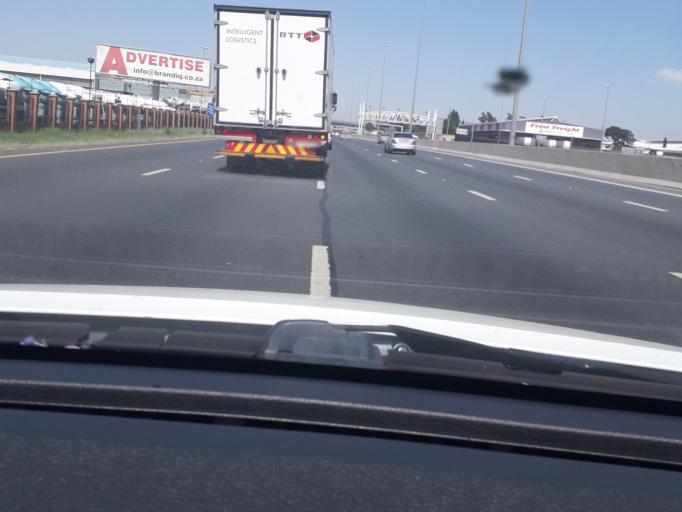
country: ZA
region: Gauteng
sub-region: Ekurhuleni Metropolitan Municipality
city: Boksburg
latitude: -26.1769
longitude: 28.2230
